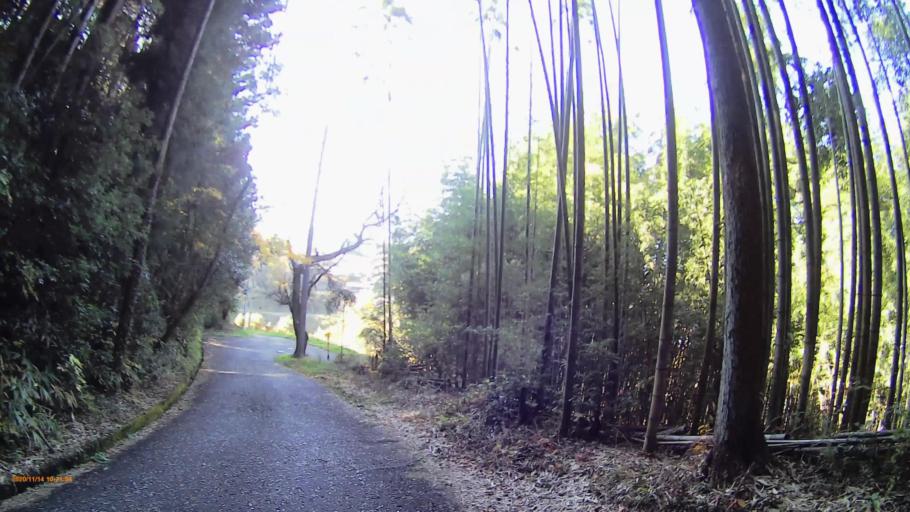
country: JP
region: Gifu
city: Nakatsugawa
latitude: 35.5110
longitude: 137.5369
